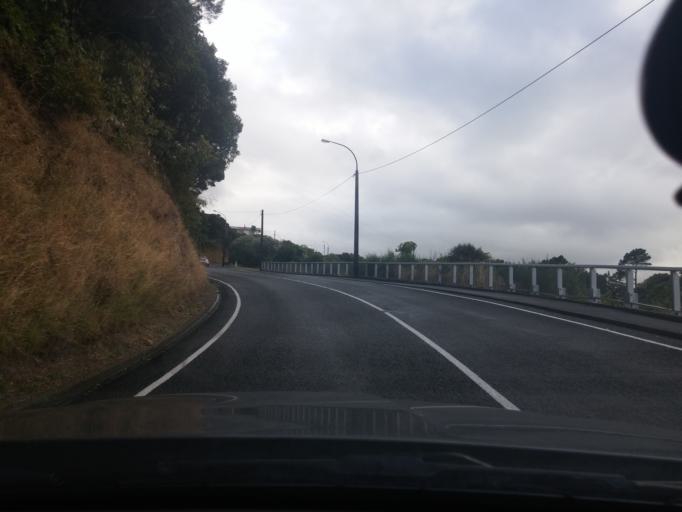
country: NZ
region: Wellington
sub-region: Wellington City
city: Kelburn
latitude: -41.2619
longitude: 174.7636
